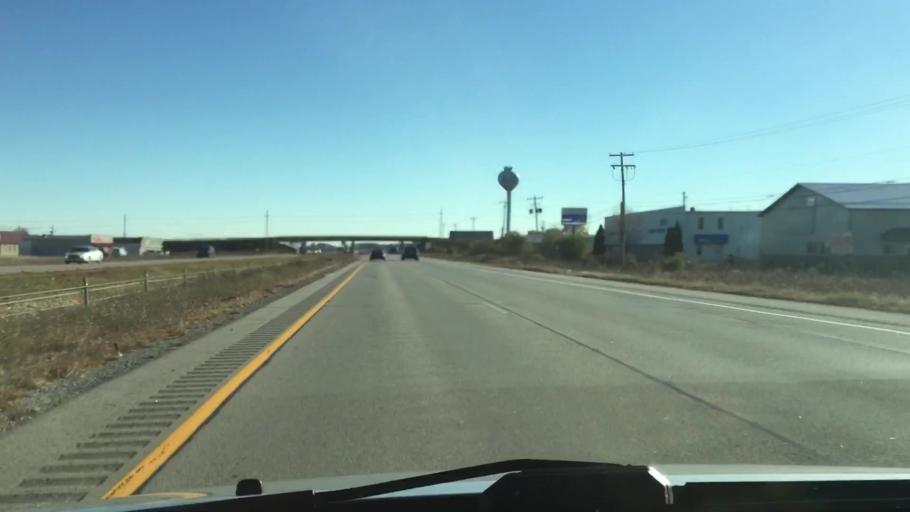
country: US
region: Wisconsin
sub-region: Outagamie County
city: Little Chute
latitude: 44.2977
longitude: -88.3076
